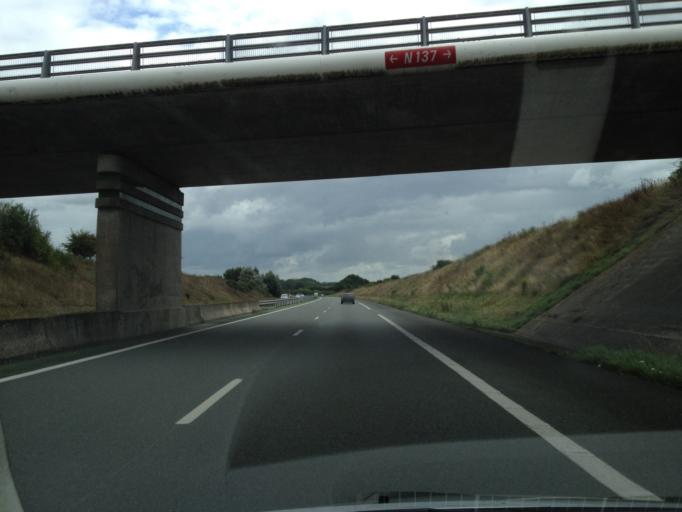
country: FR
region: Pays de la Loire
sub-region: Departement de la Vendee
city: Saint-Fulgent
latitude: 46.8348
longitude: -1.1603
